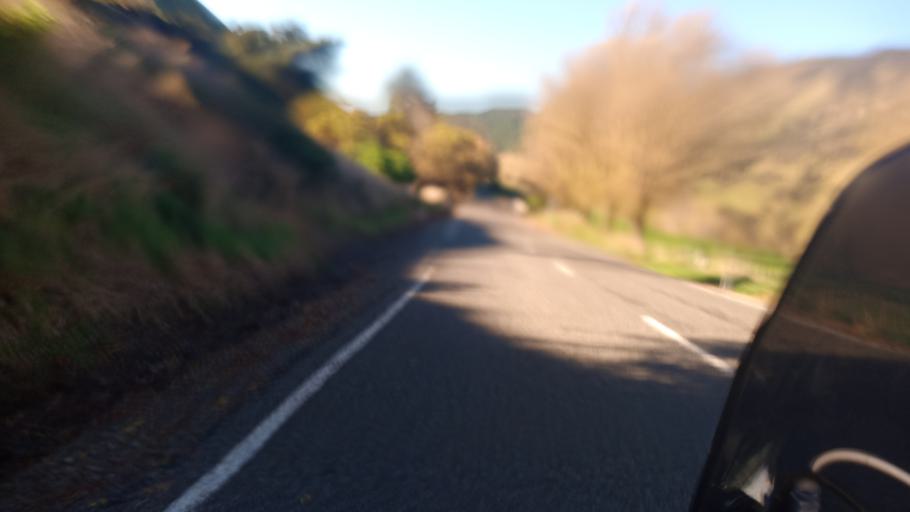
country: NZ
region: Hawke's Bay
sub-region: Wairoa District
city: Wairoa
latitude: -38.8721
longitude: 177.2144
